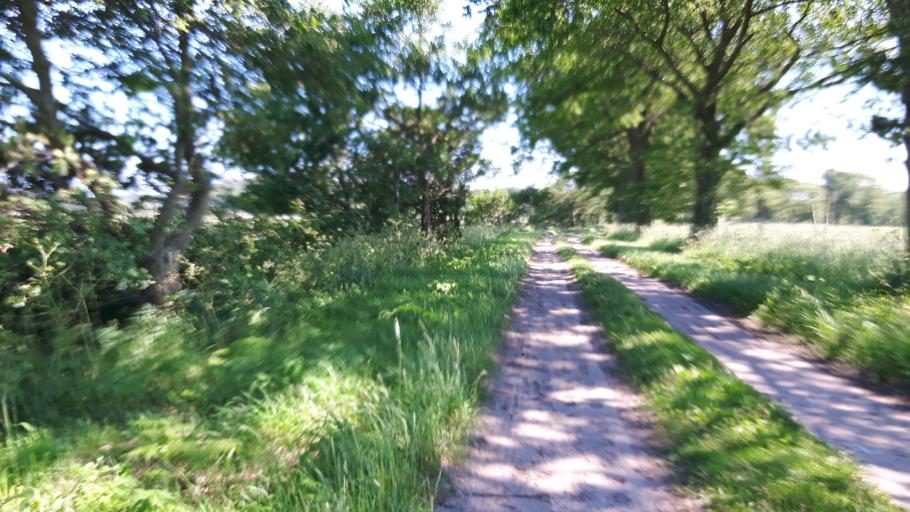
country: PL
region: Pomeranian Voivodeship
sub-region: Powiat slupski
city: Glowczyce
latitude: 54.6445
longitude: 17.3534
